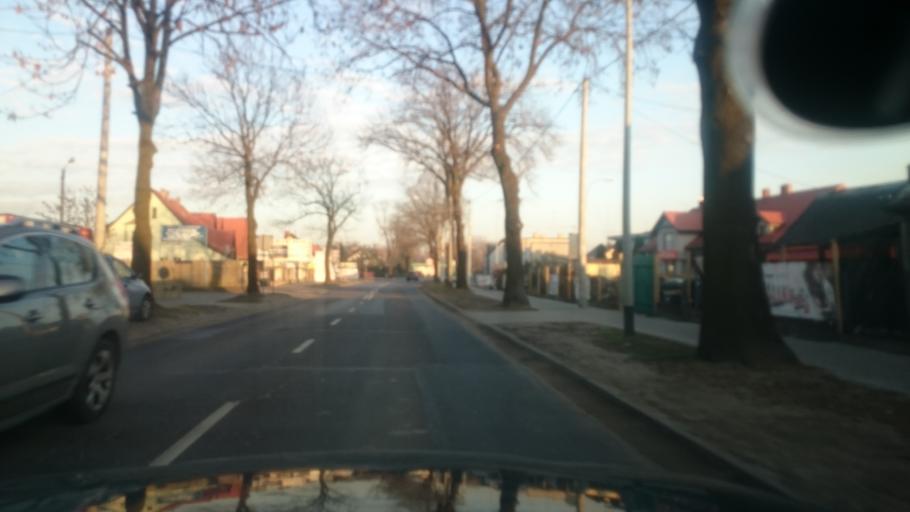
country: PL
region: Greater Poland Voivodeship
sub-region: Powiat ostrowski
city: Ostrow Wielkopolski
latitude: 51.6481
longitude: 17.8474
